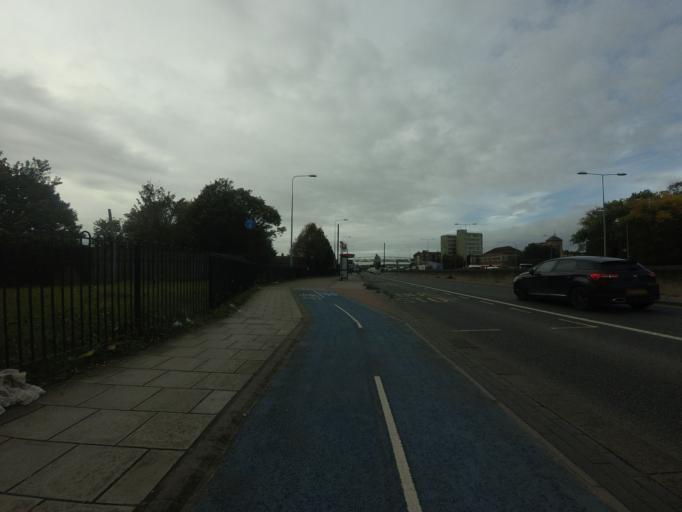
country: GB
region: England
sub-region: Greater London
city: Barking
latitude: 51.5294
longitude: 0.0910
